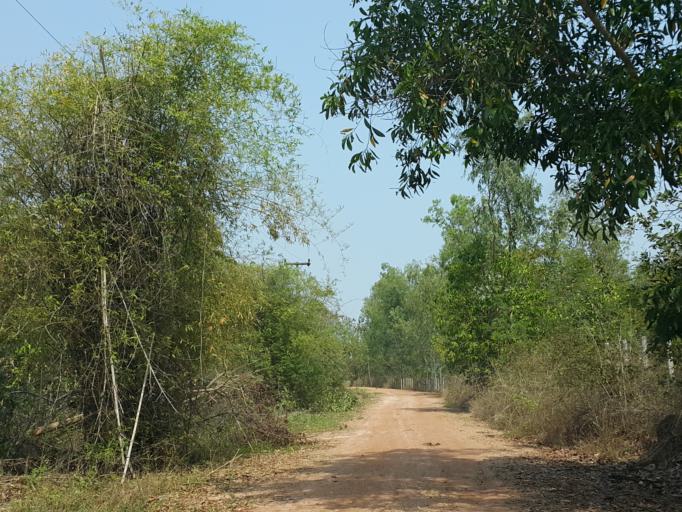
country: TH
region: Lampang
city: Hang Chat
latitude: 18.3067
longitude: 99.4173
